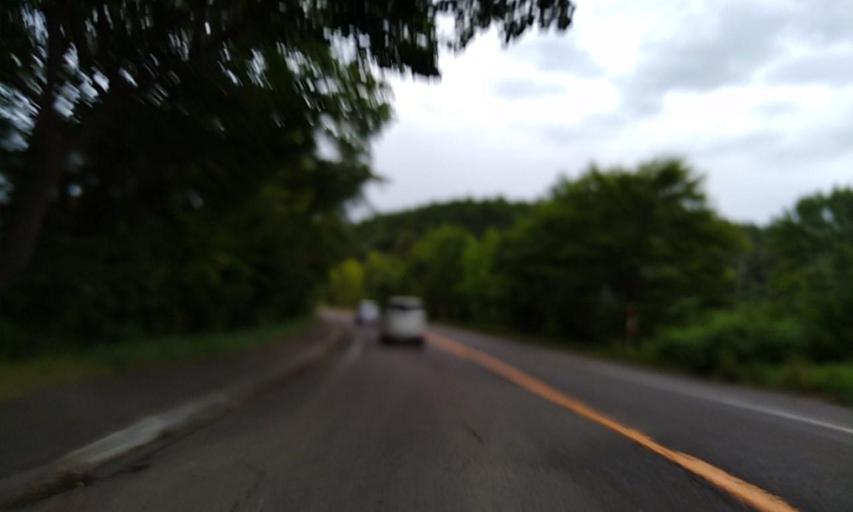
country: JP
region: Hokkaido
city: Abashiri
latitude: 43.9834
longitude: 144.2199
